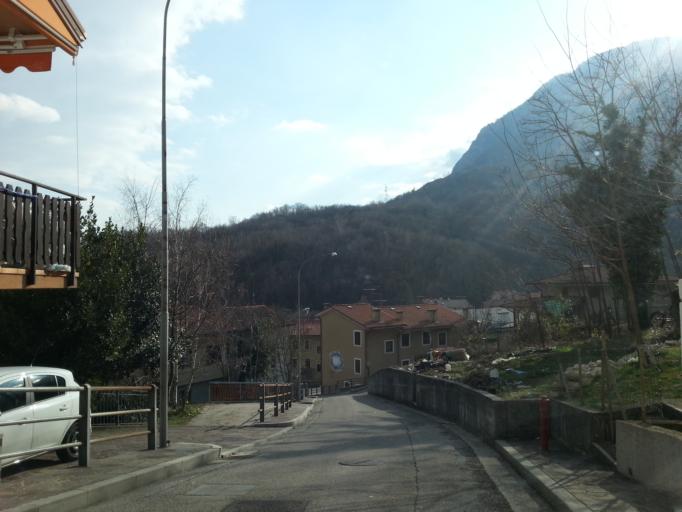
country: IT
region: Friuli Venezia Giulia
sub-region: Provincia di Udine
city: Bordano
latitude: 46.3169
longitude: 13.1030
